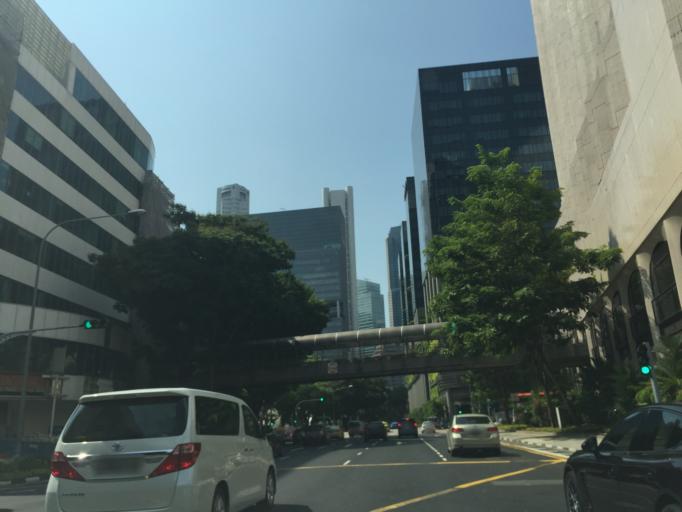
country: SG
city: Singapore
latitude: 1.2870
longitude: 103.8445
